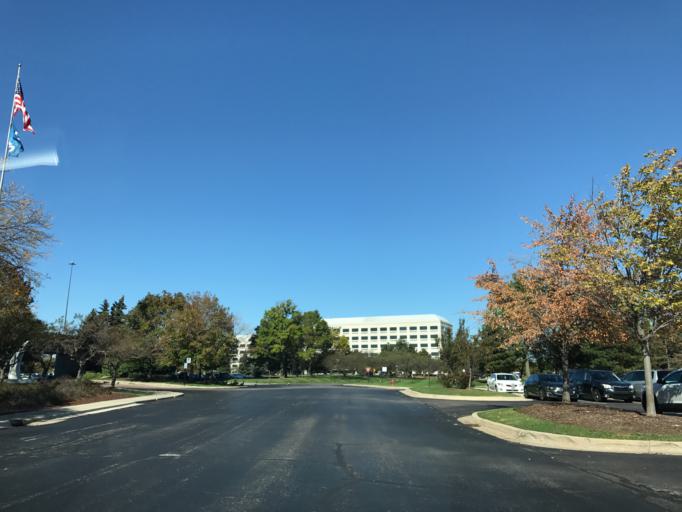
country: US
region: Michigan
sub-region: Oakland County
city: Franklin
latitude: 42.4902
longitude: -83.2984
